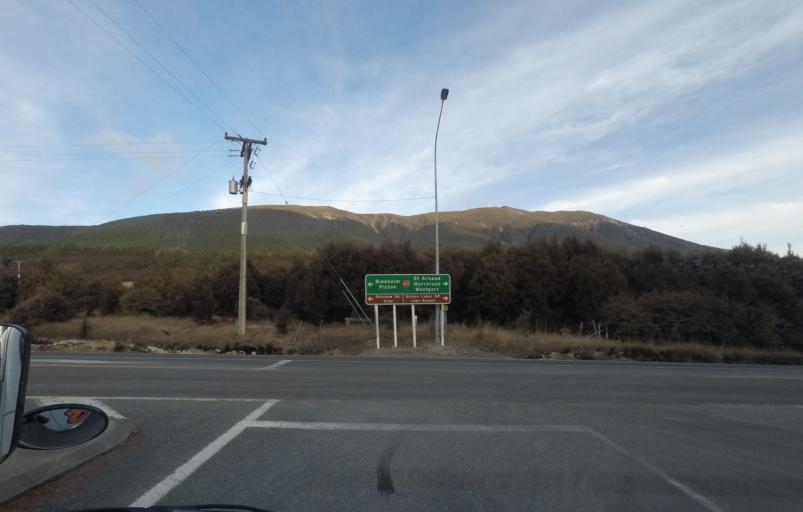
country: NZ
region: Tasman
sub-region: Tasman District
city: Wakefield
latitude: -41.7851
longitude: 172.8937
